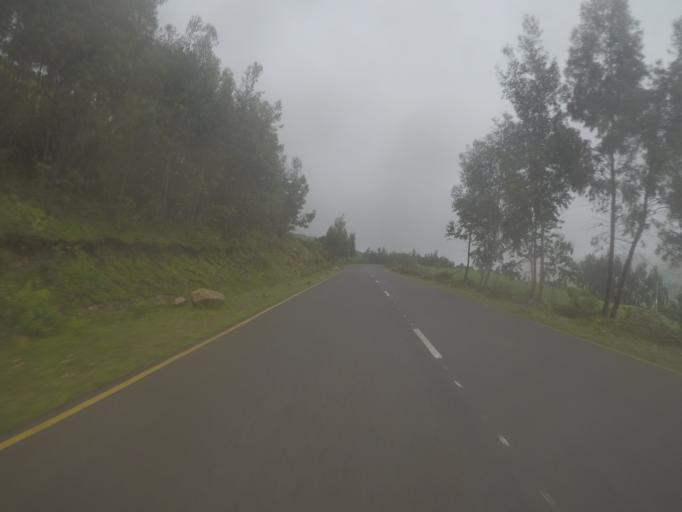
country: ET
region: Amhara
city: Gondar
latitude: 12.7443
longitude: 37.5236
